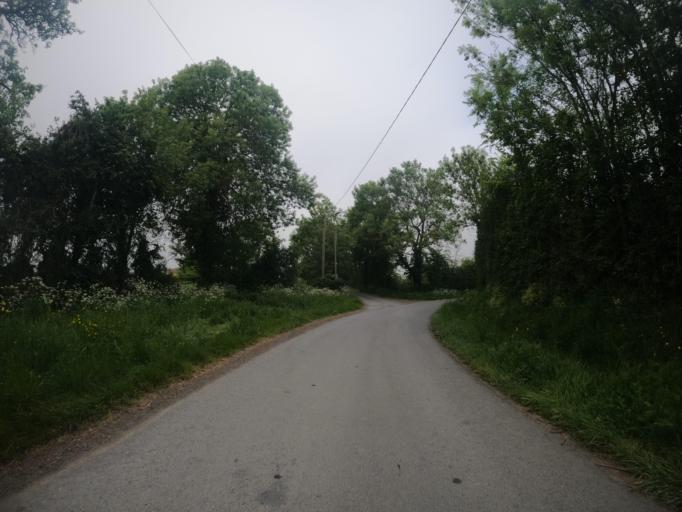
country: FR
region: Poitou-Charentes
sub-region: Departement des Deux-Sevres
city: Mauze-Thouarsais
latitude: 46.8982
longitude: -0.3318
